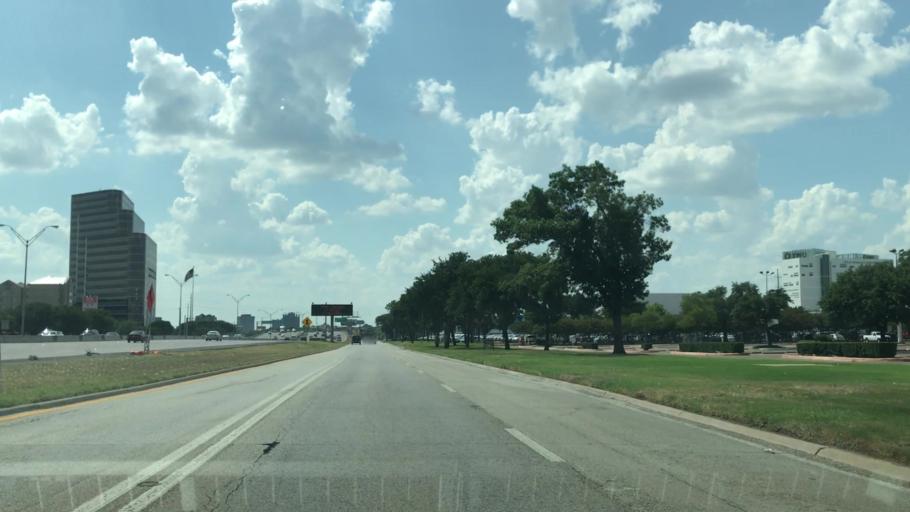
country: US
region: Texas
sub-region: Dallas County
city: Dallas
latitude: 32.8087
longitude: -96.8439
